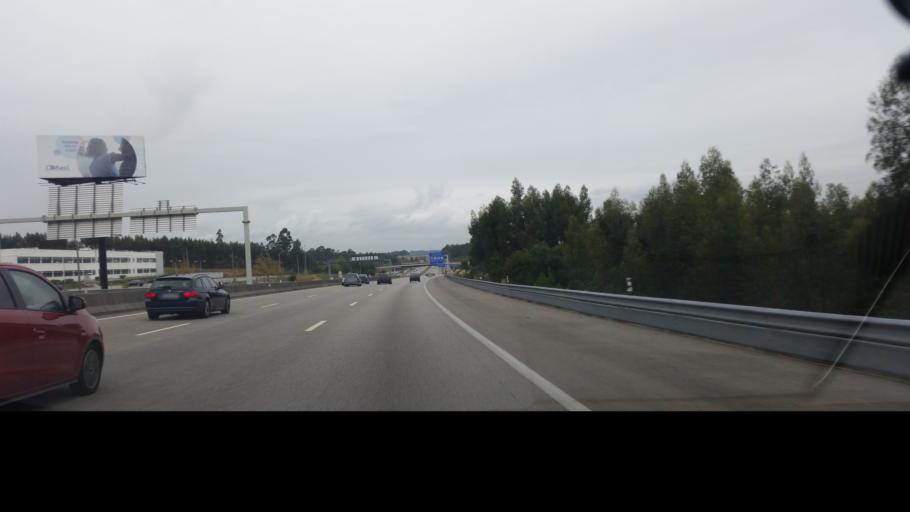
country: PT
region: Porto
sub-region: Maia
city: Nogueira
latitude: 41.2572
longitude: -8.5674
